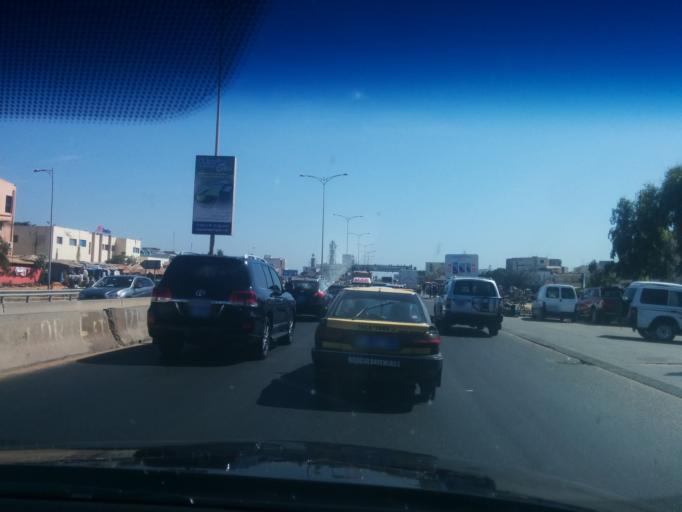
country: SN
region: Dakar
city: Grand Dakar
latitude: 14.7437
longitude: -17.4473
